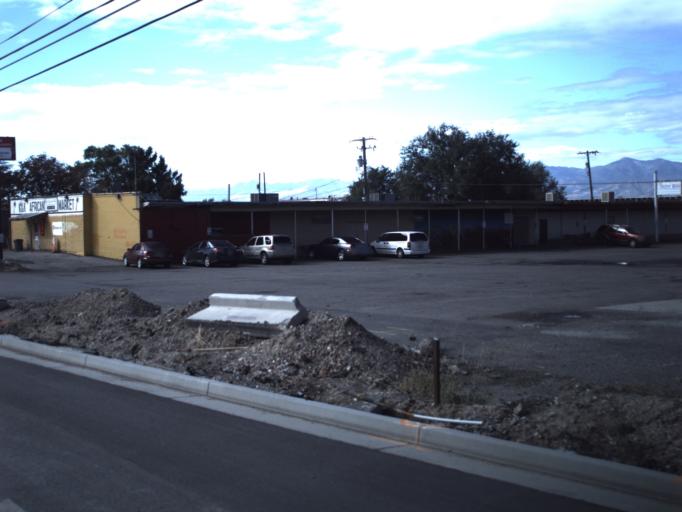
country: US
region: Utah
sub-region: Salt Lake County
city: Salt Lake City
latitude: 40.7480
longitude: -111.9391
